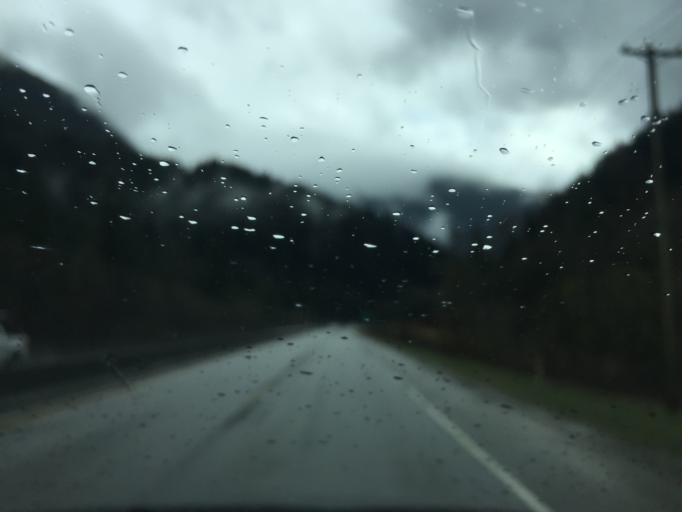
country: CA
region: British Columbia
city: Hope
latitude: 49.4057
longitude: -121.3168
